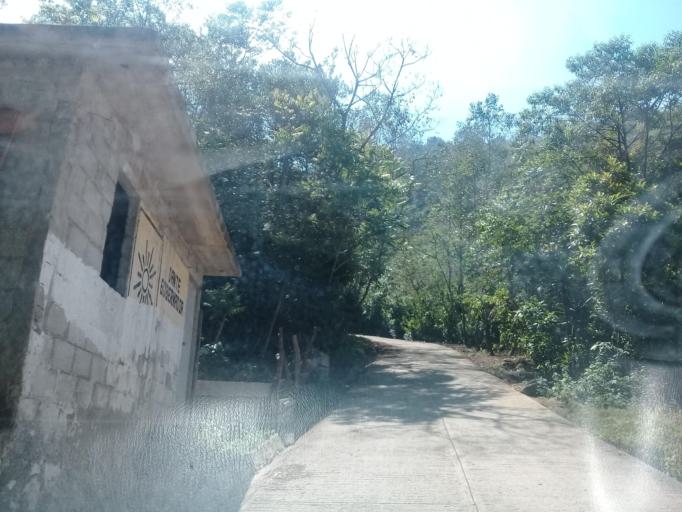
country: MX
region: Veracruz
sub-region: Tlilapan
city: Tonalixco
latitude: 18.7580
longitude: -97.0395
